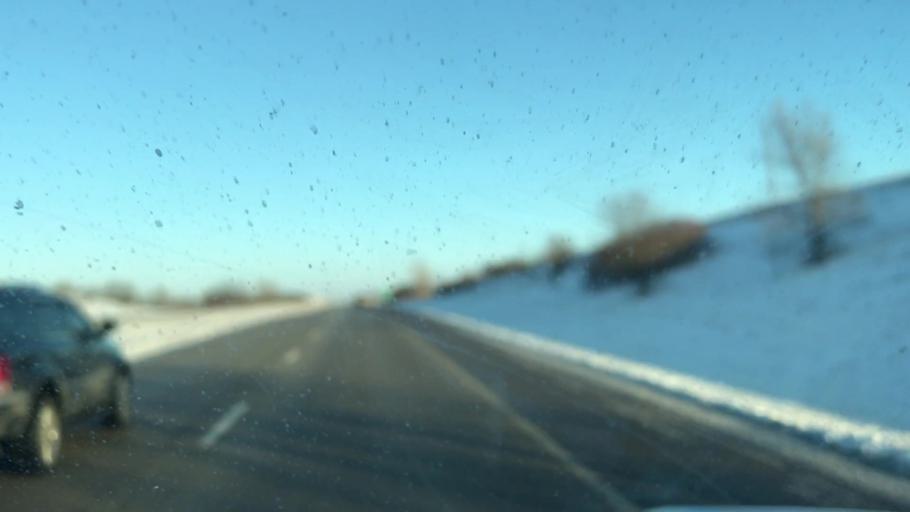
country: US
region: Missouri
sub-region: Buchanan County
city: Saint Joseph
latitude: 39.7477
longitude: -94.7061
